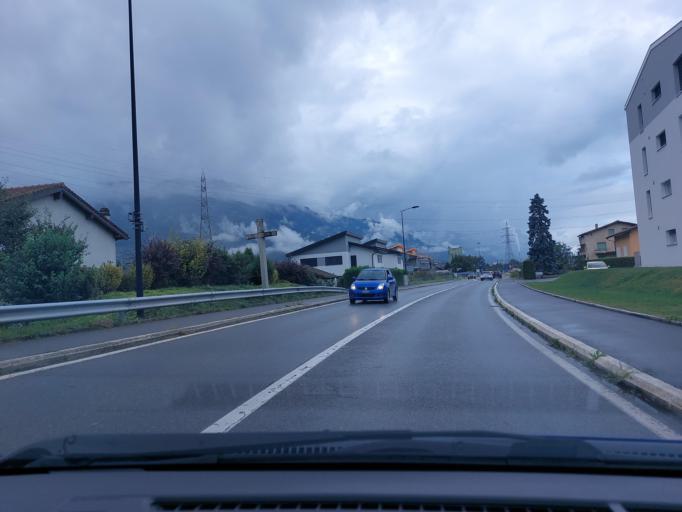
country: CH
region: Valais
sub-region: Monthey District
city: Monthey
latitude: 46.2437
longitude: 6.9838
